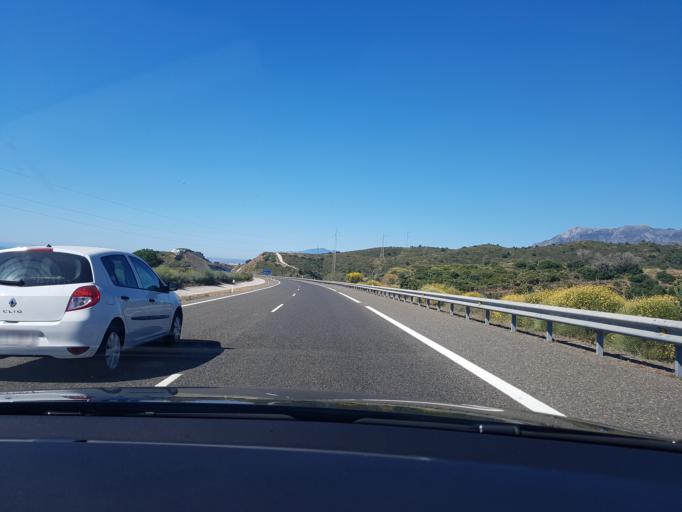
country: ES
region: Andalusia
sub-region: Provincia de Malaga
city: Ojen
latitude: 36.5175
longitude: -4.8084
